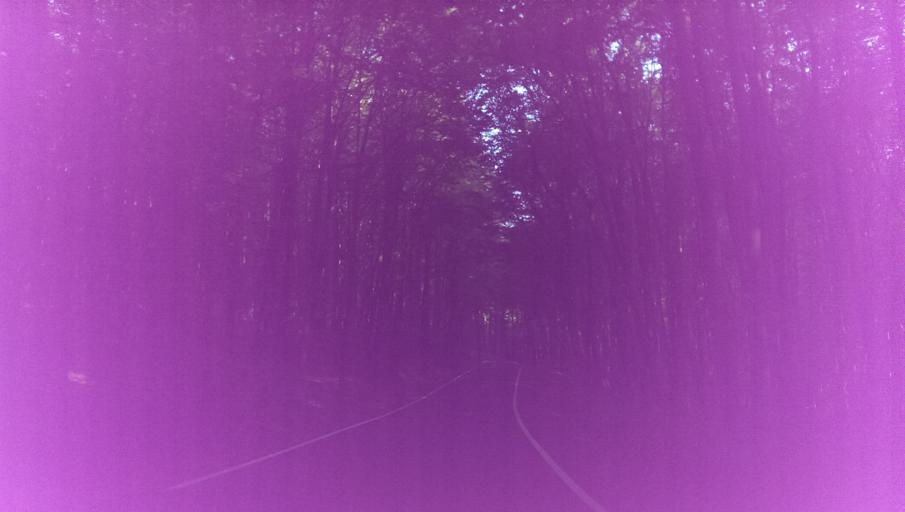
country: CZ
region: South Moravian
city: Zeravice
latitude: 49.0775
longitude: 17.2156
